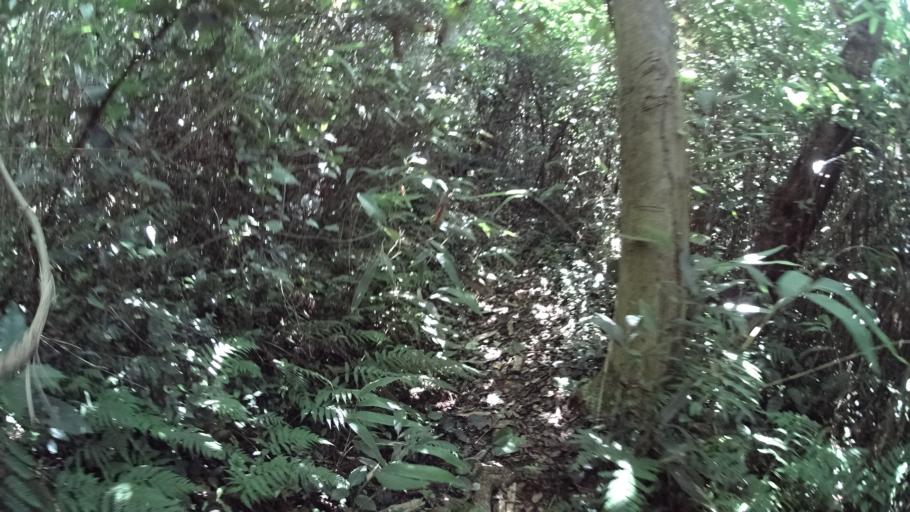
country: JP
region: Shizuoka
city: Shimoda
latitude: 34.5164
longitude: 139.2767
